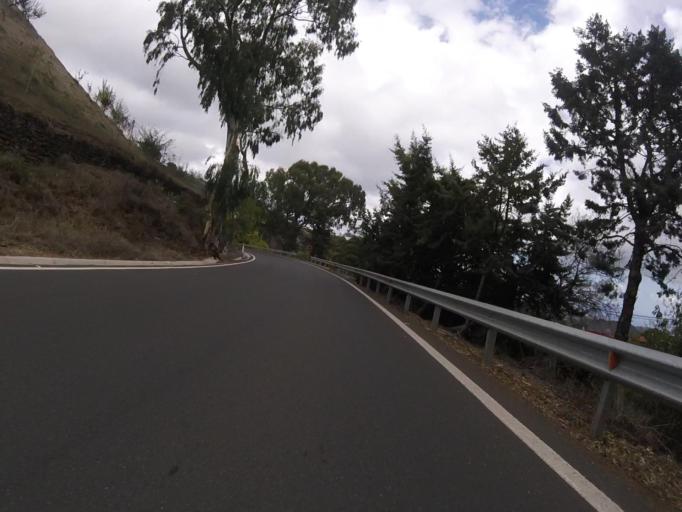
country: ES
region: Canary Islands
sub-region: Provincia de Las Palmas
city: Vega de San Mateo
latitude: 28.0047
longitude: -15.5575
